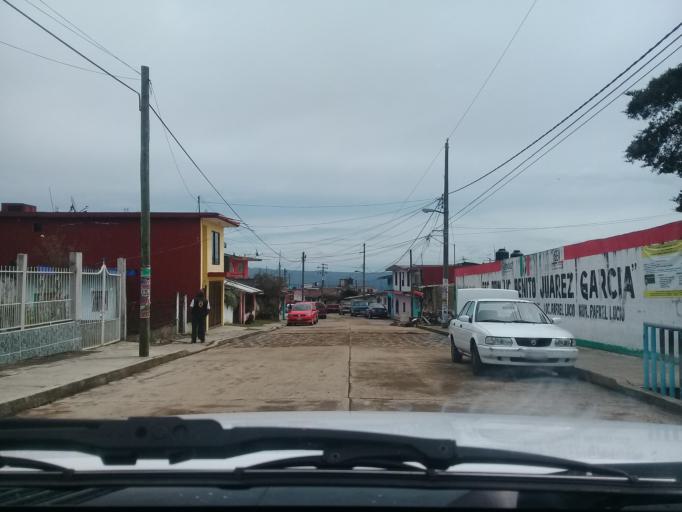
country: MX
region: Veracruz
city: Rafael Lucio
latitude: 19.5910
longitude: -96.9910
